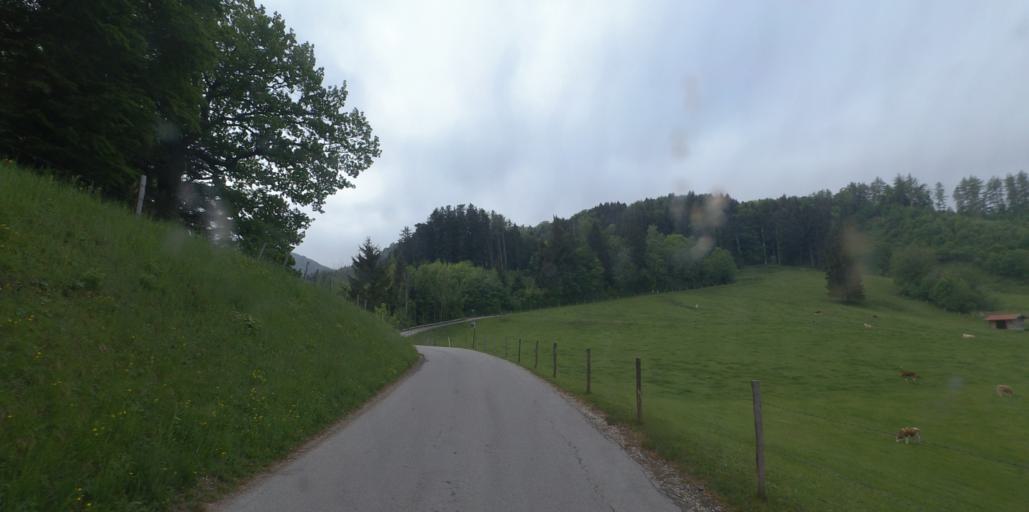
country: DE
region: Bavaria
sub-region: Upper Bavaria
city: Bernau am Chiemsee
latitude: 47.7960
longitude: 12.3608
